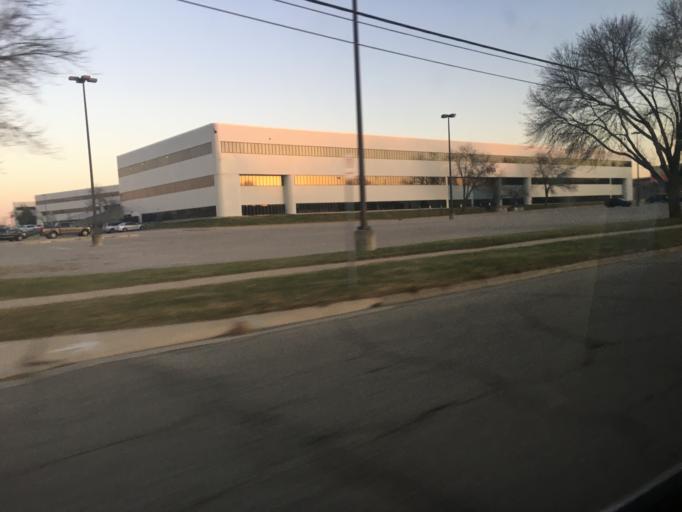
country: US
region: Minnesota
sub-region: Olmsted County
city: Rochester
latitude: 44.0671
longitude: -92.5089
